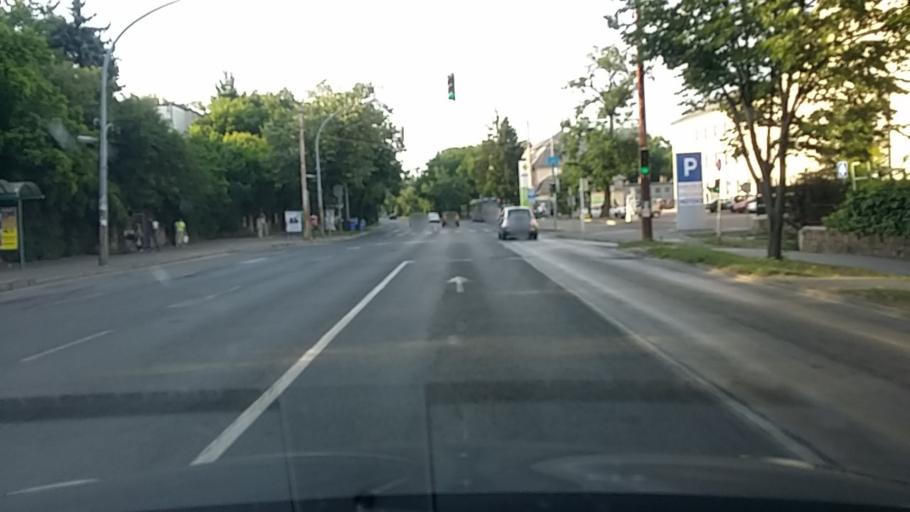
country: HU
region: Borsod-Abauj-Zemplen
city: Miskolc
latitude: 48.0901
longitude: 20.7858
